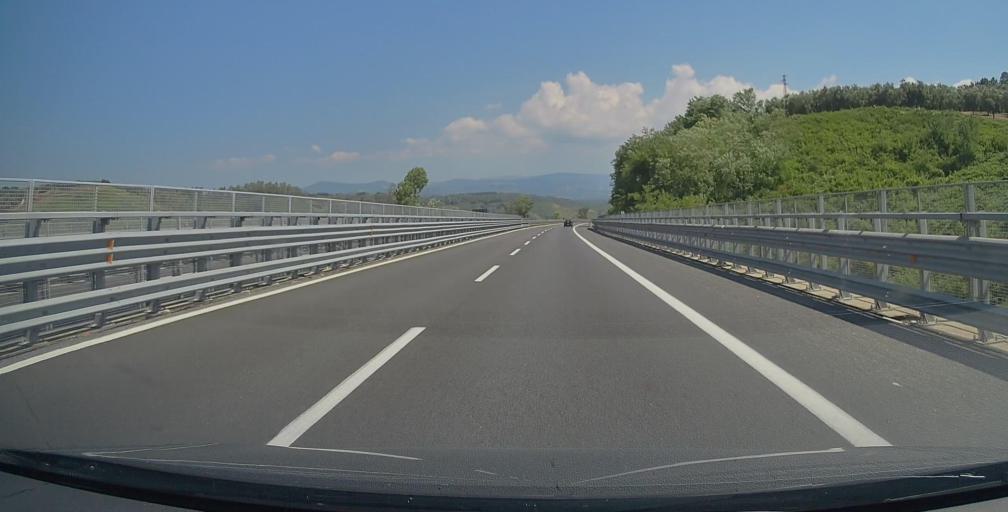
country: IT
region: Calabria
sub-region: Provincia di Vibo-Valentia
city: Maierato
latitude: 38.6779
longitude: 16.1748
